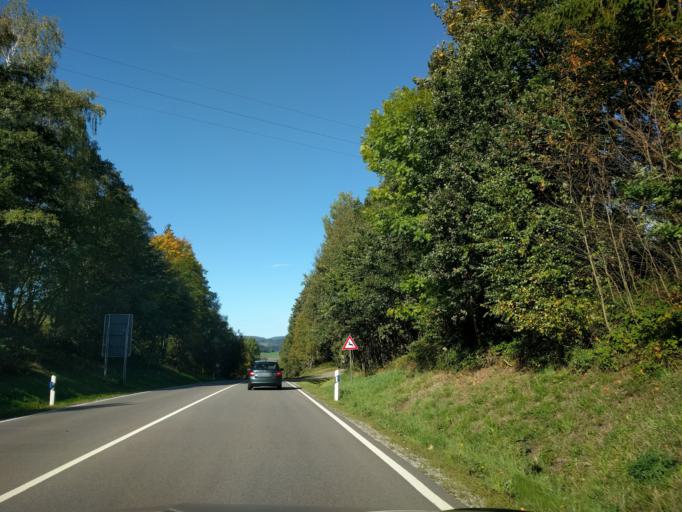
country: DE
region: Bavaria
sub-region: Lower Bavaria
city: Geiersthal
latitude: 49.0353
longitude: 12.9568
